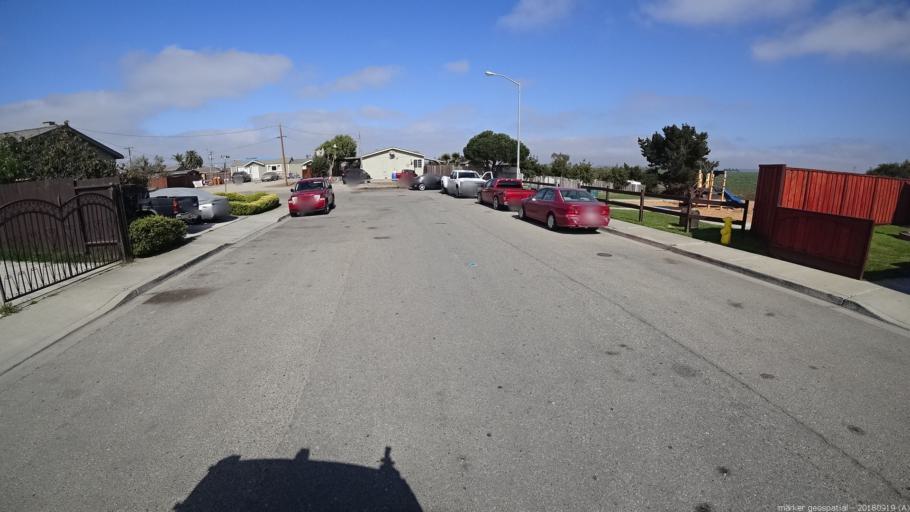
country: US
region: California
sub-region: Monterey County
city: Castroville
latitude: 36.7706
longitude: -121.7508
